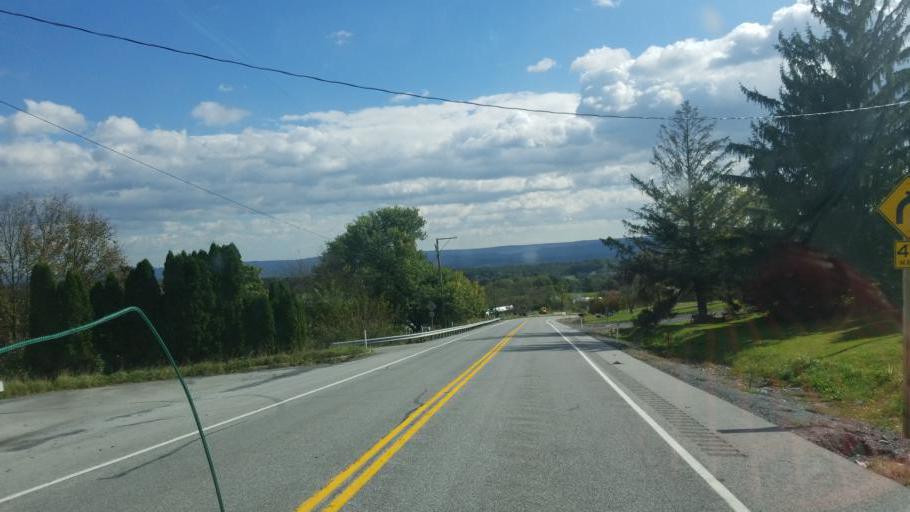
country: US
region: Pennsylvania
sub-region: Fulton County
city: McConnellsburg
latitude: 40.0130
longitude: -78.1151
